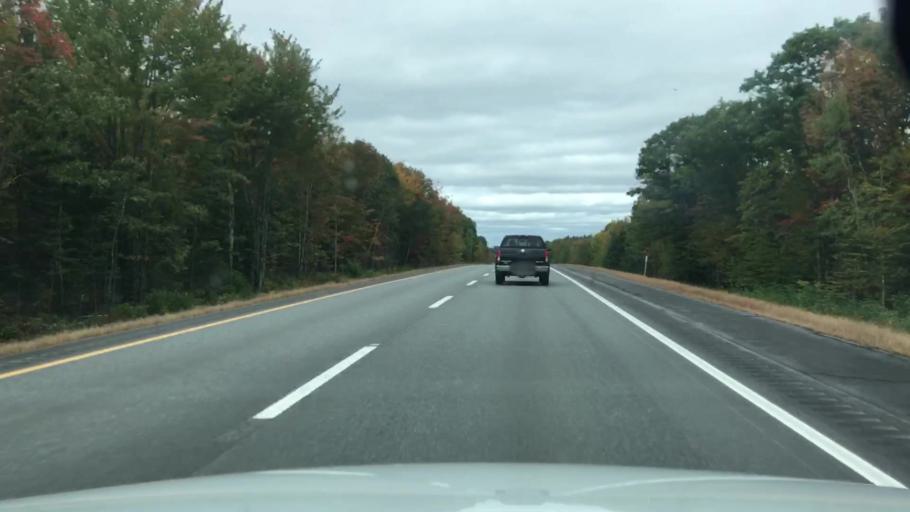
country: US
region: Maine
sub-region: Somerset County
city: Pittsfield
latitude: 44.7617
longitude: -69.4145
